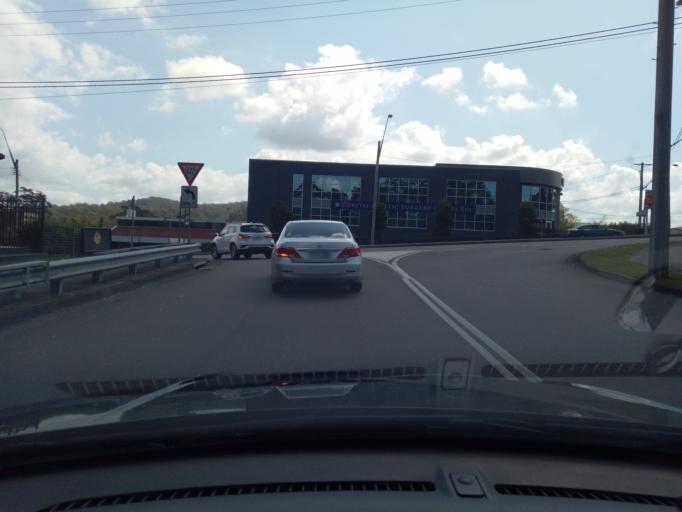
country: AU
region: New South Wales
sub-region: Gosford Shire
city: Erina
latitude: -33.4346
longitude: 151.3891
